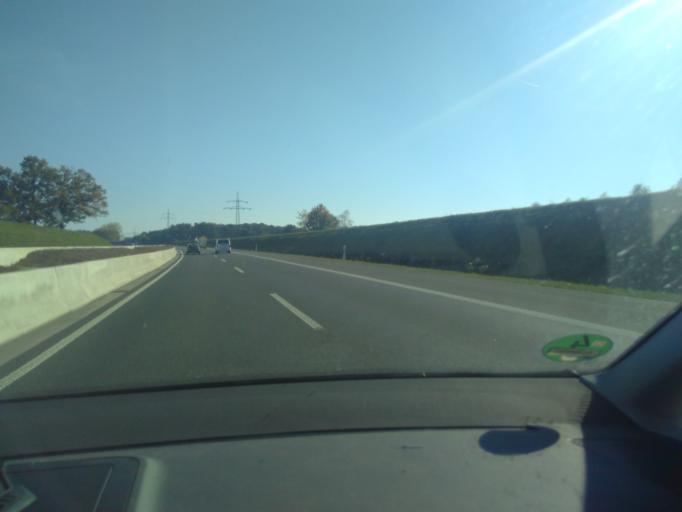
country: DE
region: North Rhine-Westphalia
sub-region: Regierungsbezirk Detmold
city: Steinhagen
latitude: 51.9931
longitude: 8.4445
